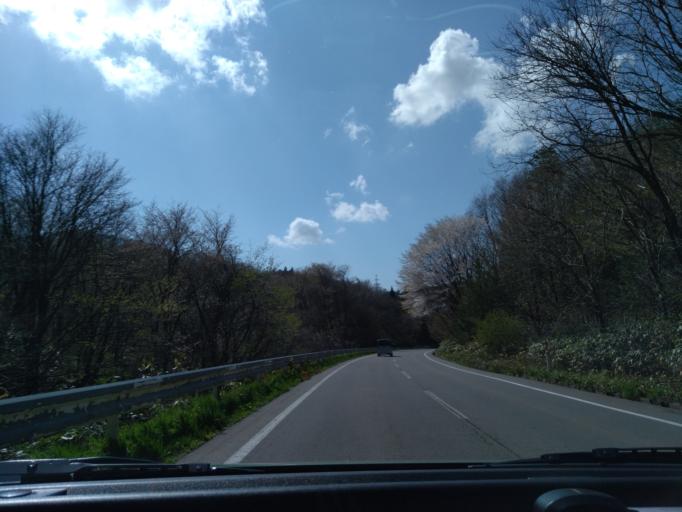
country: JP
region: Akita
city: Akita
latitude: 39.6942
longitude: 140.2407
